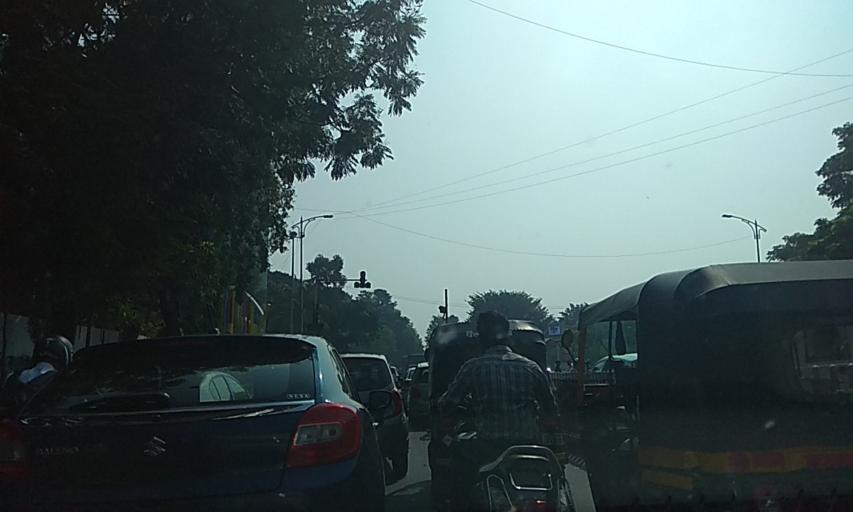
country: IN
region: Maharashtra
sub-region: Pune Division
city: Shivaji Nagar
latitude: 18.5453
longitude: 73.8765
